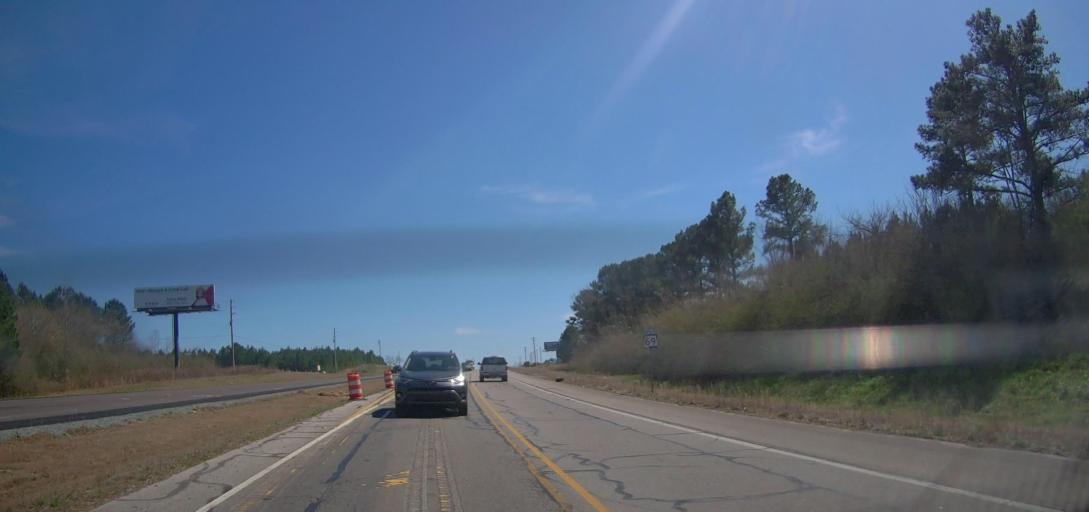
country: US
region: Alabama
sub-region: Cullman County
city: Cullman
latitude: 34.1969
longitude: -86.7905
